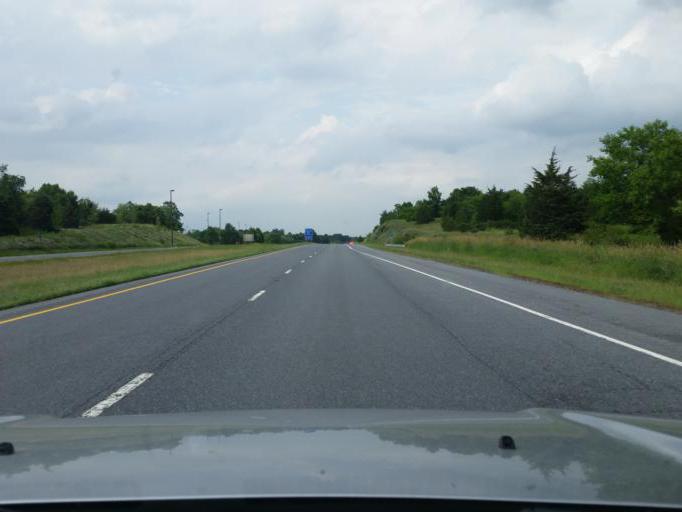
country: US
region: Maryland
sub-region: Frederick County
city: Emmitsburg
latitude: 39.7048
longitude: -77.3134
